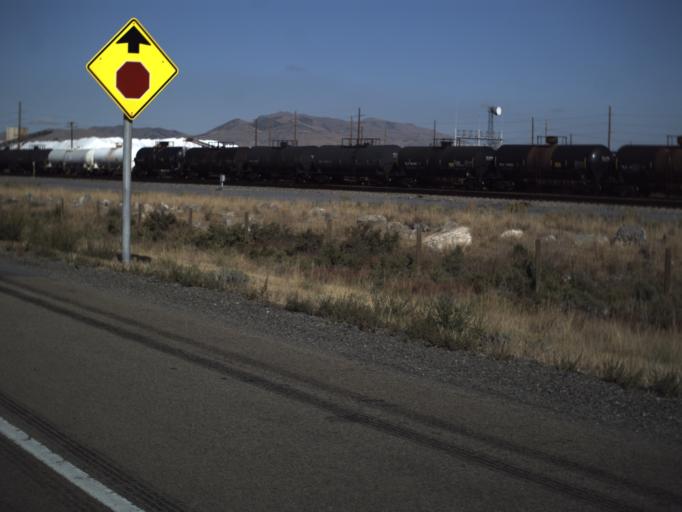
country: US
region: Utah
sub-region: Tooele County
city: Grantsville
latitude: 40.7459
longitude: -112.6492
